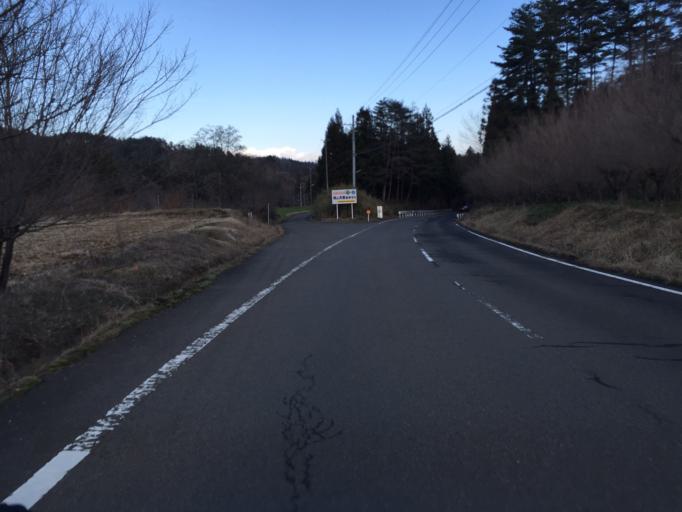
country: JP
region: Fukushima
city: Fukushima-shi
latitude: 37.7032
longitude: 140.3934
